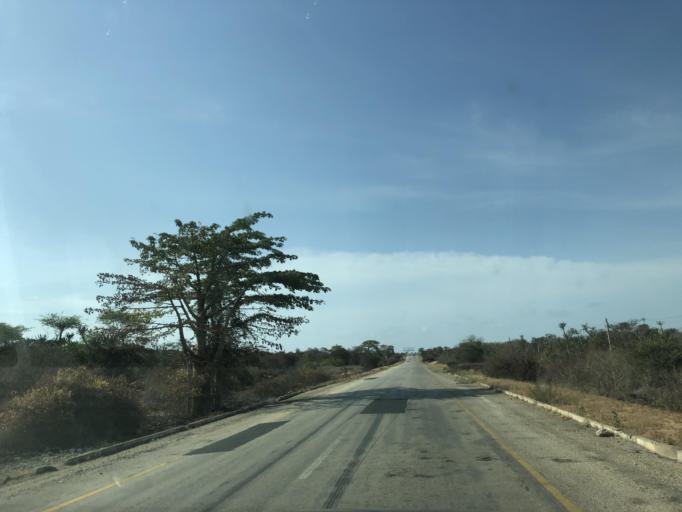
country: AO
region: Luanda
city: Luanda
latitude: -9.3682
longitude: 13.1785
